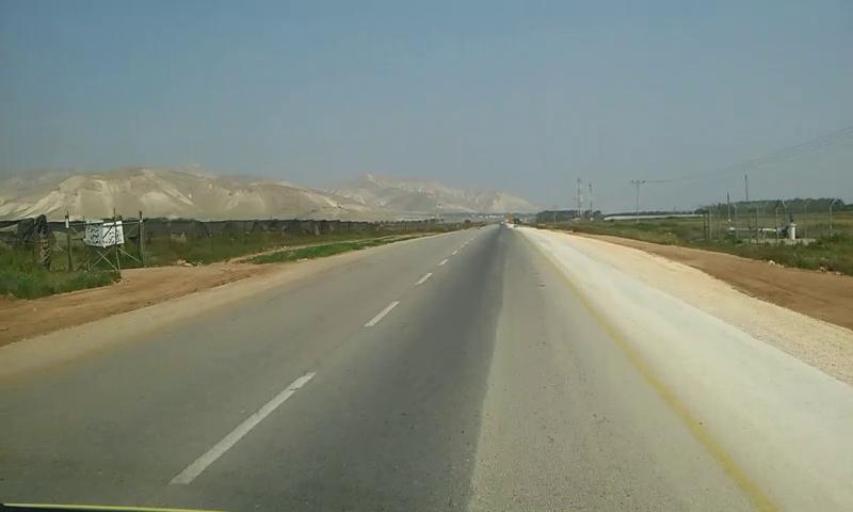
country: PS
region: West Bank
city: Al Fasayil
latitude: 32.0366
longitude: 35.4563
